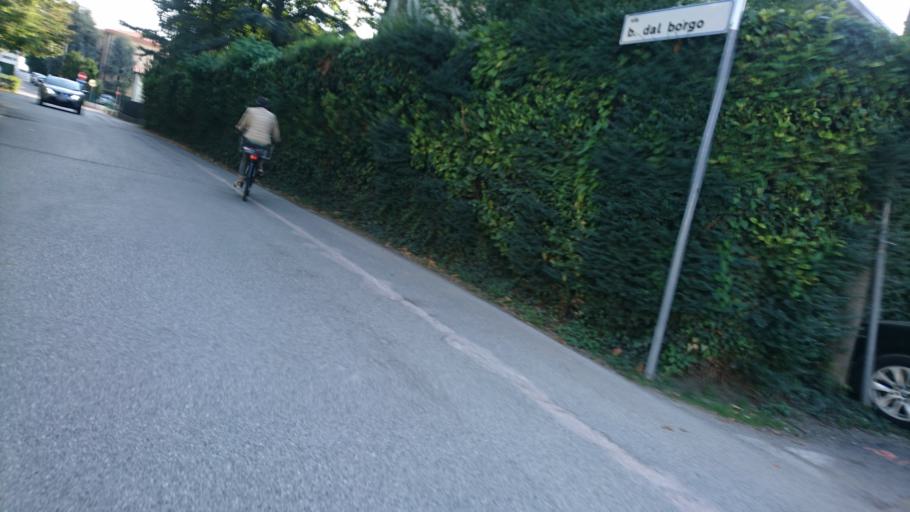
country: IT
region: Veneto
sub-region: Provincia di Padova
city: Padova
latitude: 45.3895
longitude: 11.8758
